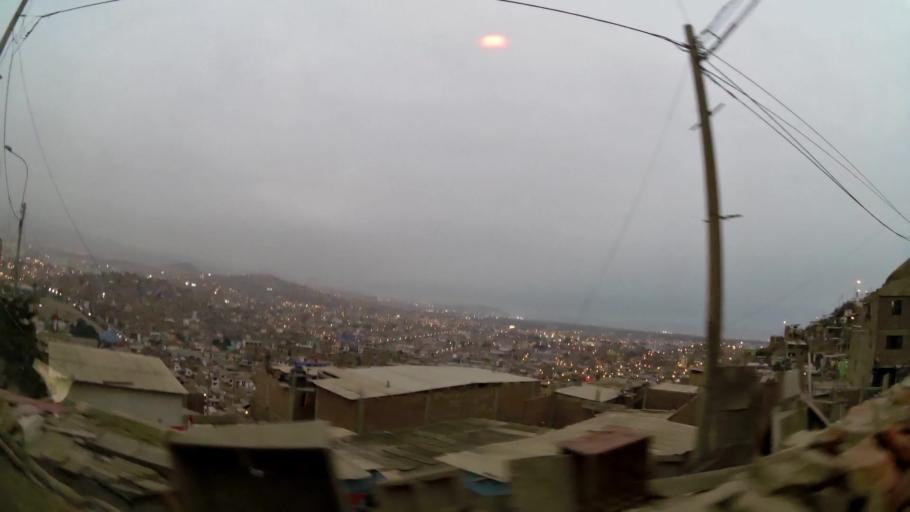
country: PE
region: Lima
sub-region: Lima
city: Surco
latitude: -12.1868
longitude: -77.0208
